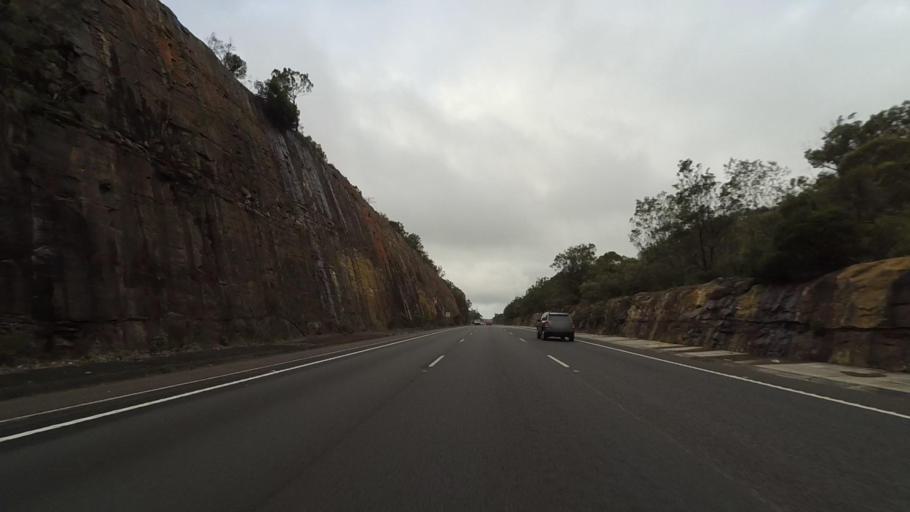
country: AU
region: New South Wales
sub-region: Wollongong
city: Bulli
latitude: -34.2977
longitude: 150.9135
